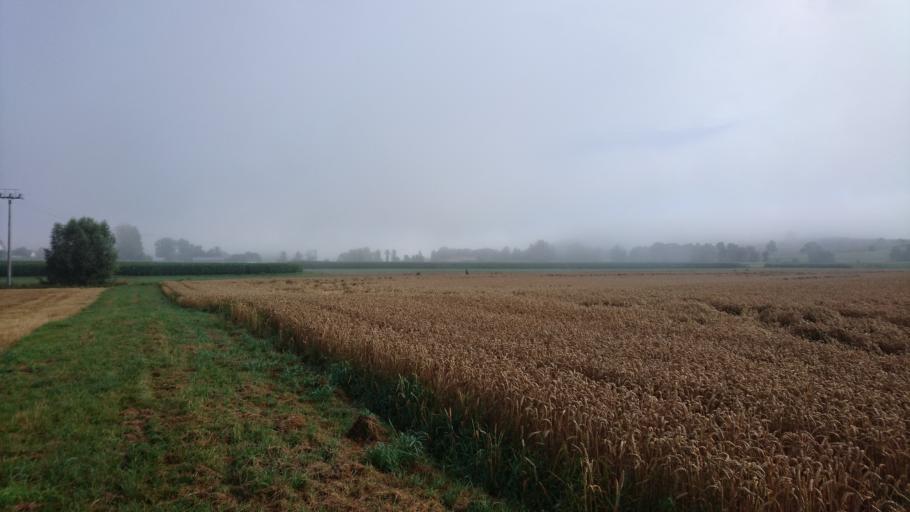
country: DE
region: Bavaria
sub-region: Swabia
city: Altenmunster
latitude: 48.4436
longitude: 10.5916
